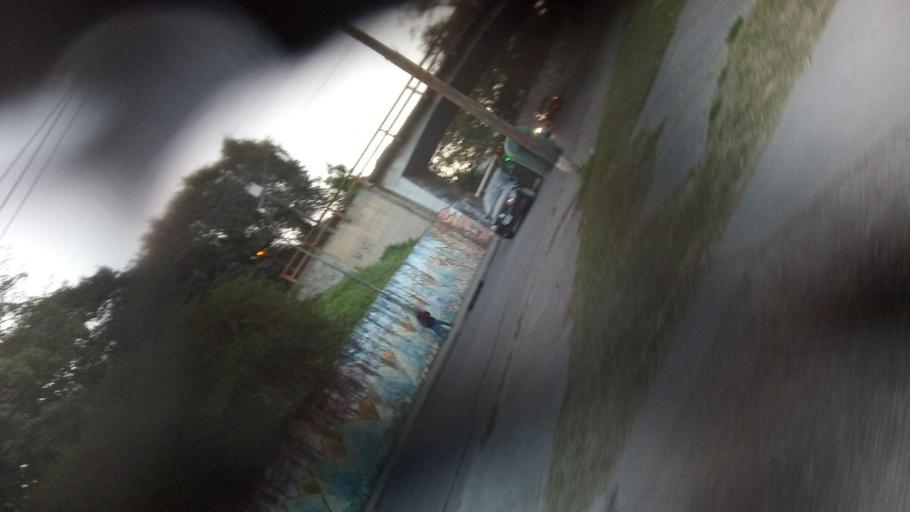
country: AR
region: Jujuy
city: San Salvador de Jujuy
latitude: -24.1891
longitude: -65.3101
